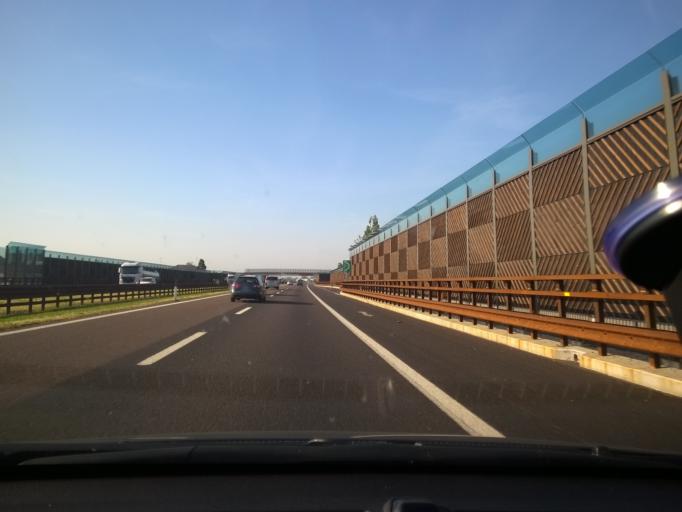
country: IT
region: Emilia-Romagna
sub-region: Provincia di Modena
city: Santa Croce Scuole
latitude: 44.7470
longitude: 10.8447
